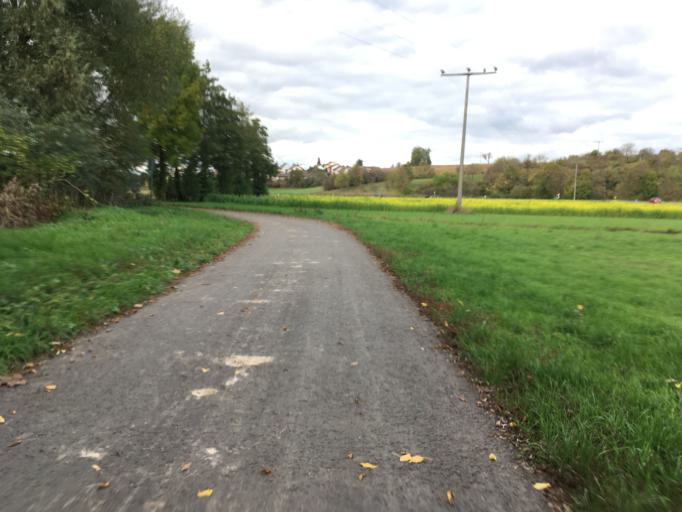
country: DE
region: Baden-Wuerttemberg
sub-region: Regierungsbezirk Stuttgart
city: Ittlingen
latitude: 49.1804
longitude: 8.9384
